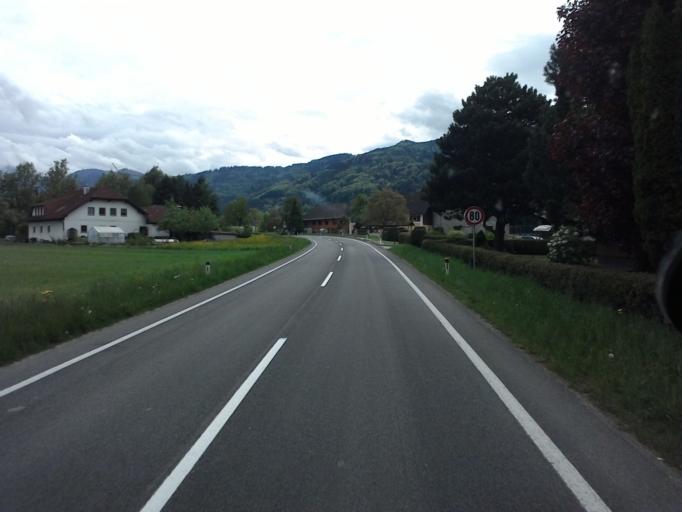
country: AT
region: Upper Austria
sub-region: Politischer Bezirk Kirchdorf an der Krems
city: Micheldorf in Oberoesterreich
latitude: 47.9371
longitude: 14.0841
